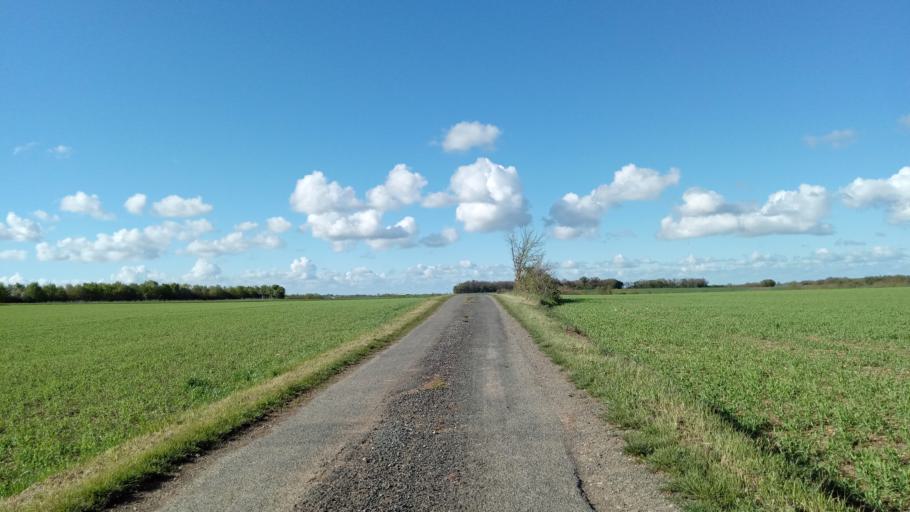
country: FR
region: Poitou-Charentes
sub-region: Departement de la Charente-Maritime
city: Verines
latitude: 46.1563
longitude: -0.9341
